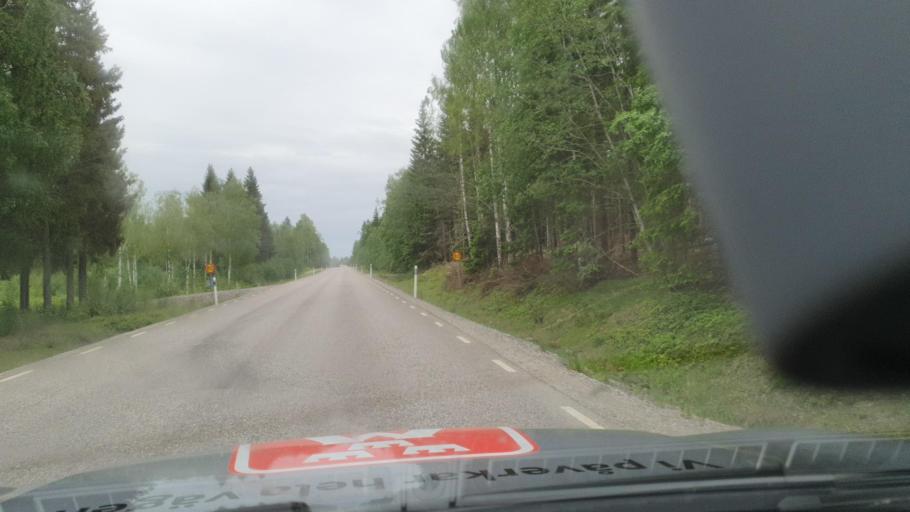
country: SE
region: Vaesternorrland
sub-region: Kramfors Kommun
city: Kramfors
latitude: 62.9212
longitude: 17.9419
